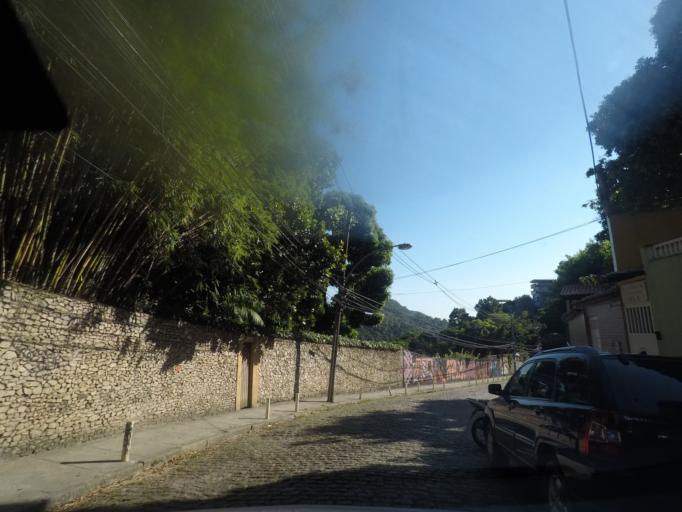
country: BR
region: Rio de Janeiro
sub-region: Rio De Janeiro
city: Rio de Janeiro
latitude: -22.9420
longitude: -43.2056
